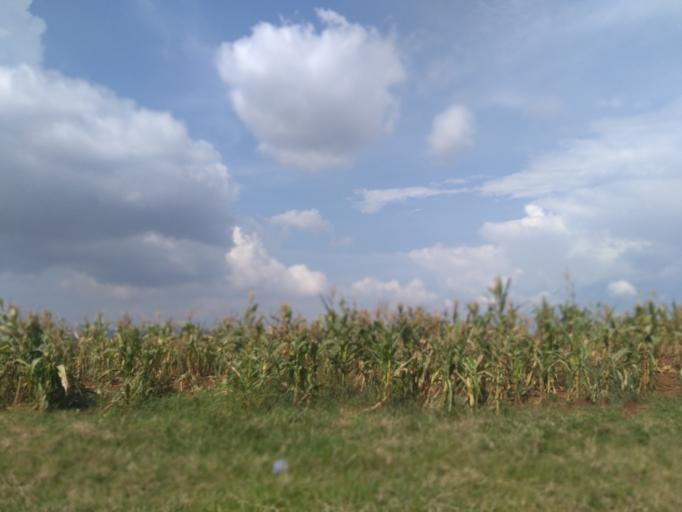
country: UG
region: Eastern Region
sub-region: Jinja District
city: Jinja
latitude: 0.4223
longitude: 33.2240
